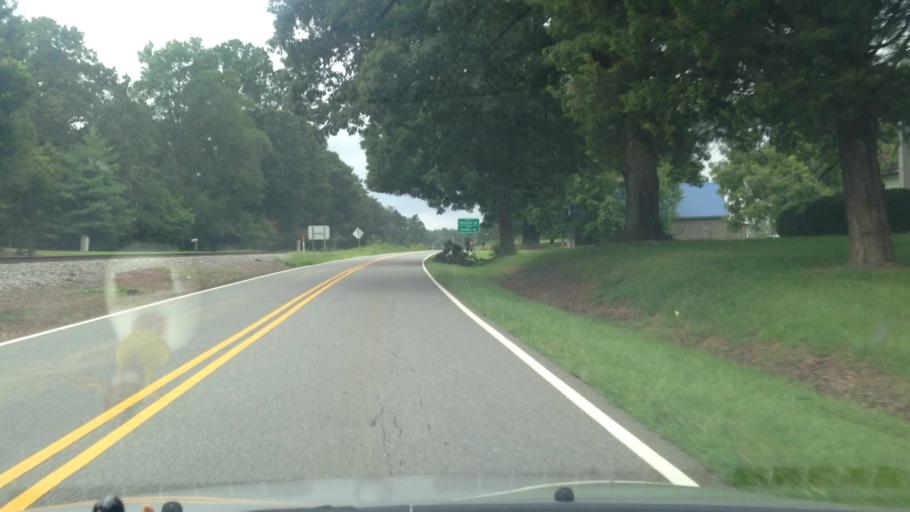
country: US
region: North Carolina
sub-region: Stokes County
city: Walnut Cove
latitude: 36.2591
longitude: -80.1471
